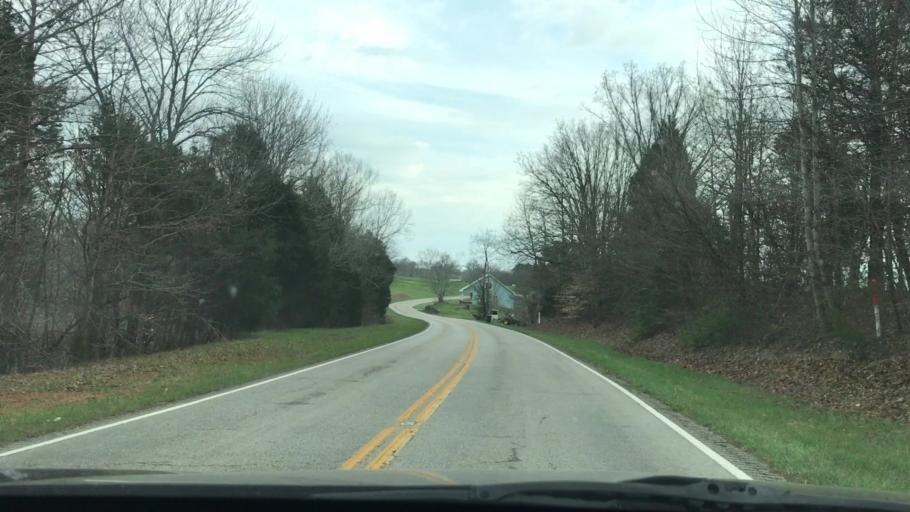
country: US
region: Kentucky
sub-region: Hart County
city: Munfordville
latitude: 37.3013
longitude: -85.7643
